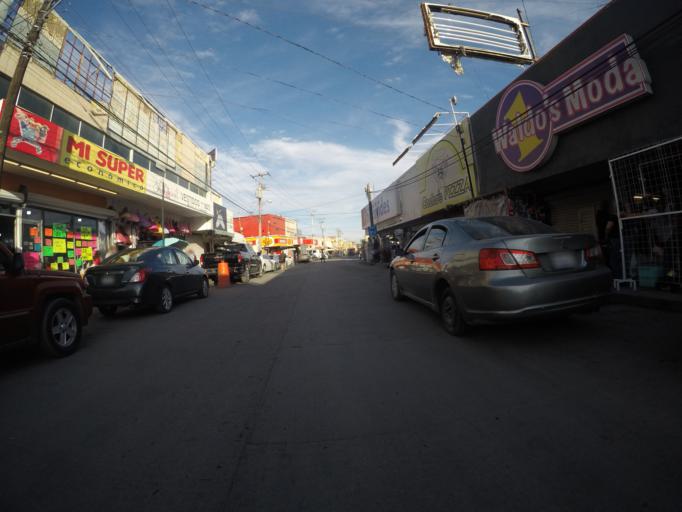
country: MX
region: Chihuahua
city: Ciudad Juarez
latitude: 31.7364
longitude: -106.4862
